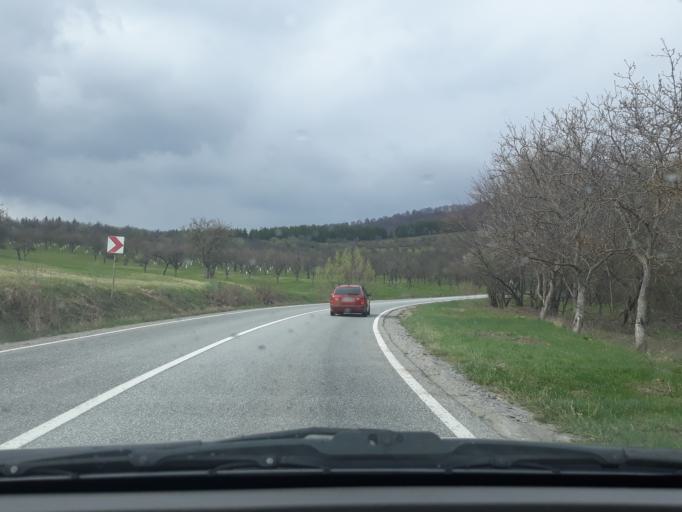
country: RO
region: Harghita
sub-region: Comuna Lupeni
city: Lupeni
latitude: 46.4057
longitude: 25.2129
